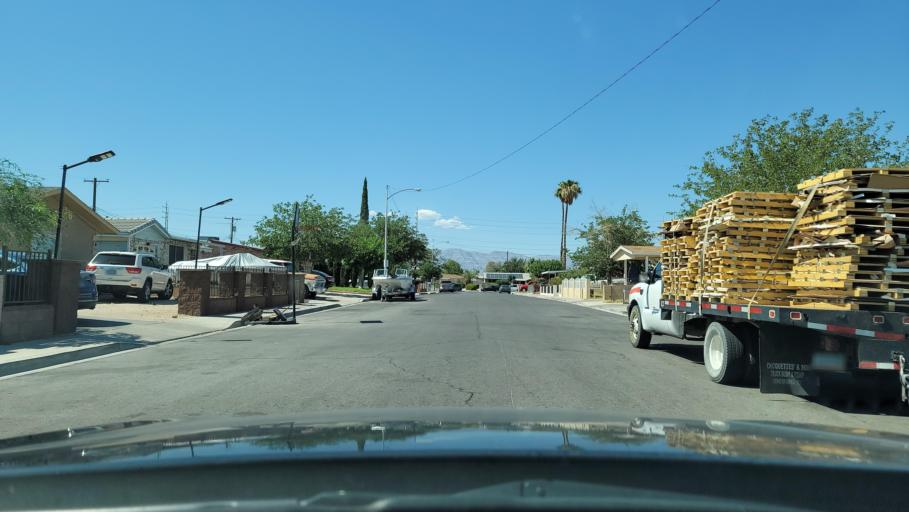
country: US
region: Nevada
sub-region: Clark County
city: Las Vegas
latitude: 36.2001
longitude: -115.1510
